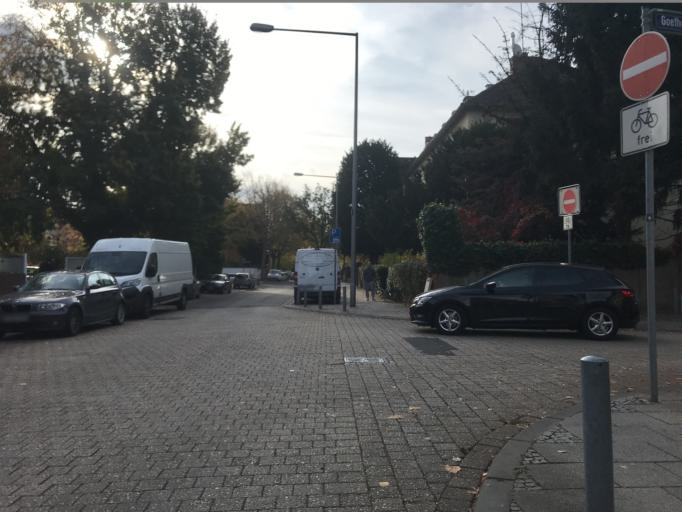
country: DE
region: Hesse
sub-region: Regierungsbezirk Darmstadt
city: Wiesbaden
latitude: 50.0377
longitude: 8.2424
